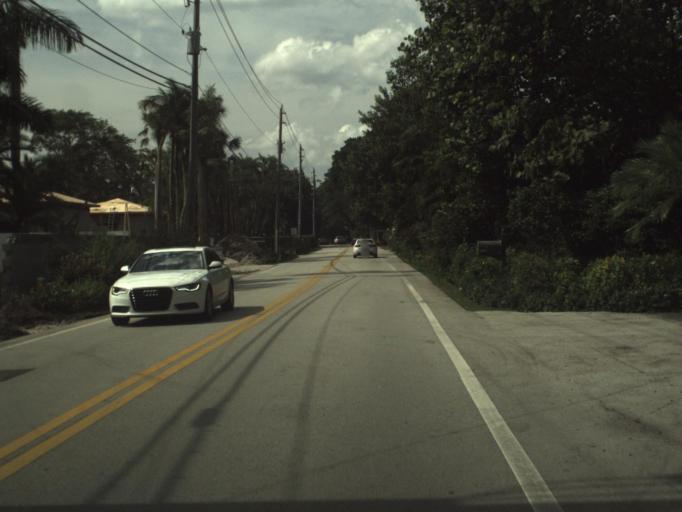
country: US
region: Florida
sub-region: Palm Beach County
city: Palm Beach
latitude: 26.6679
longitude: -80.0378
